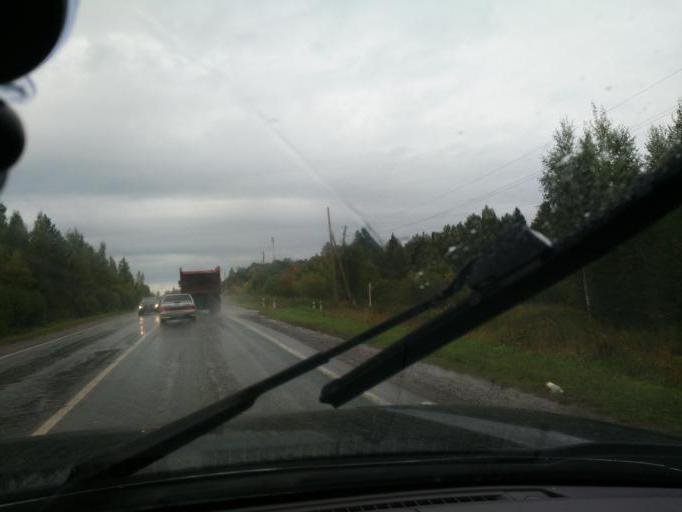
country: RU
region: Perm
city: Kultayevo
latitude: 57.8367
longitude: 55.8206
